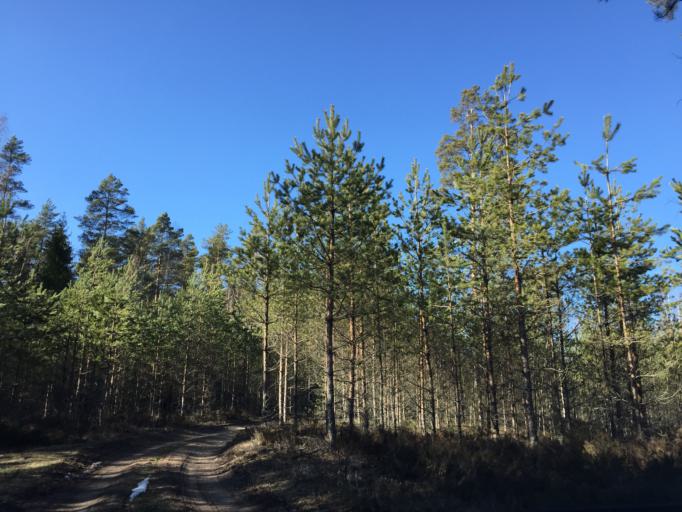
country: LV
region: Ropazu
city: Ropazi
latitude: 56.8925
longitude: 24.7049
